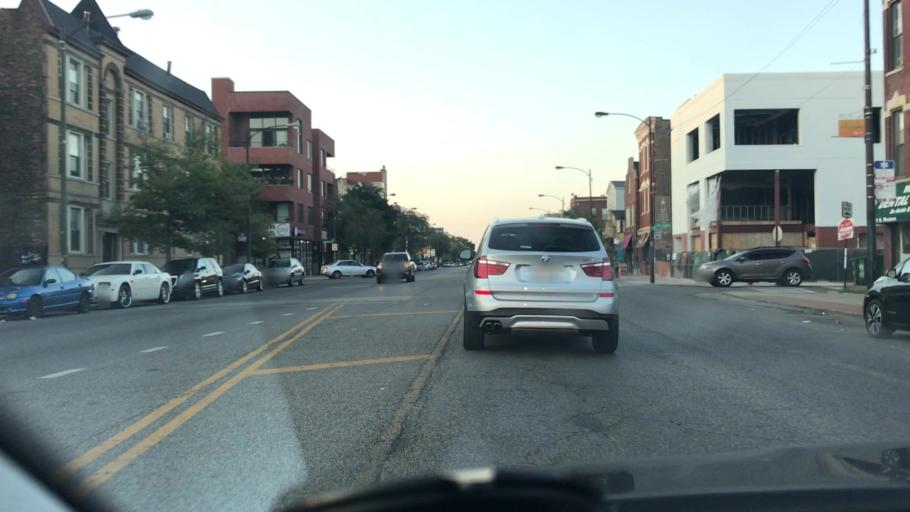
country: US
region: Illinois
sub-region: Cook County
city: Chicago
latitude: 41.9180
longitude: -87.6874
